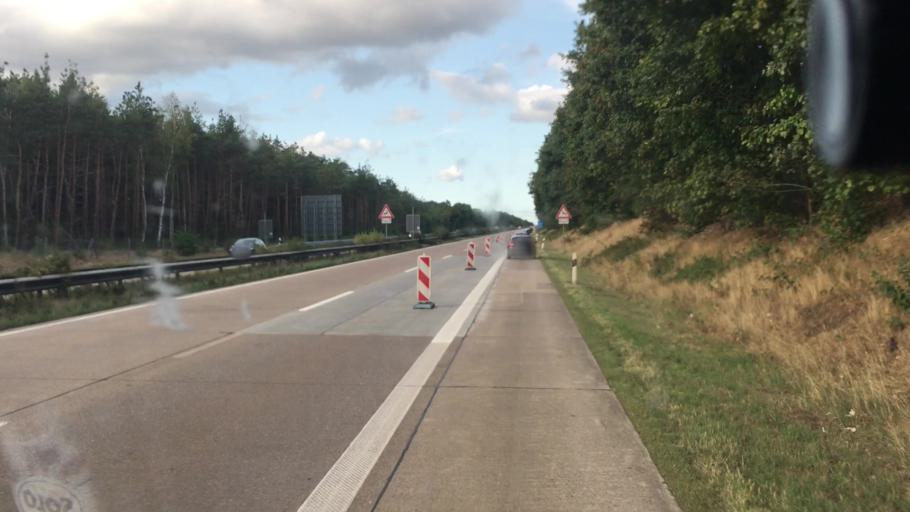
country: DE
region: Lower Saxony
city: Wardenburg
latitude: 53.0650
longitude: 8.2364
